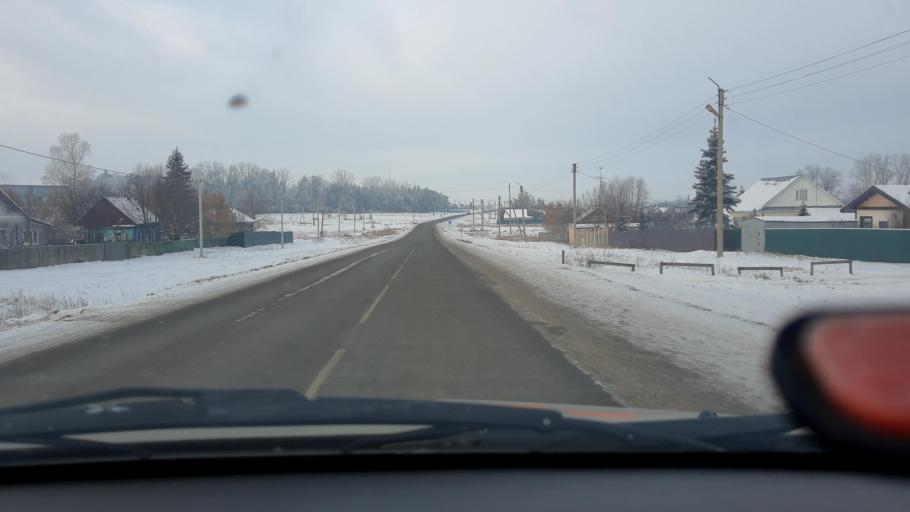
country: RU
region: Bashkortostan
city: Avdon
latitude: 54.3746
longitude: 55.8127
